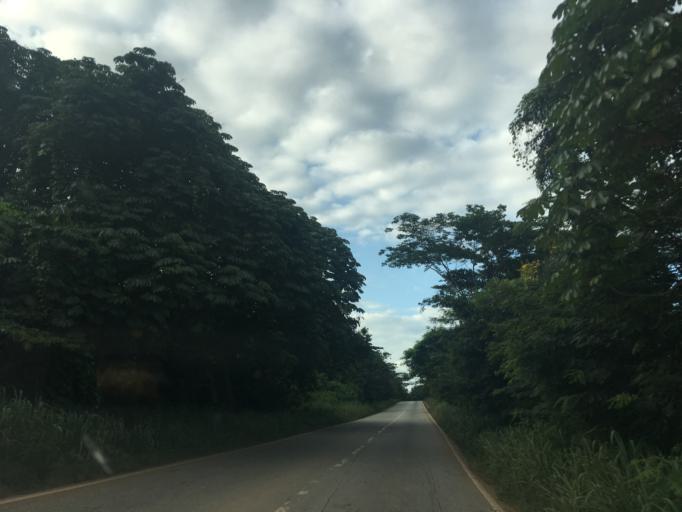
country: GH
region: Western
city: Bibiani
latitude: 6.4148
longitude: -2.3028
